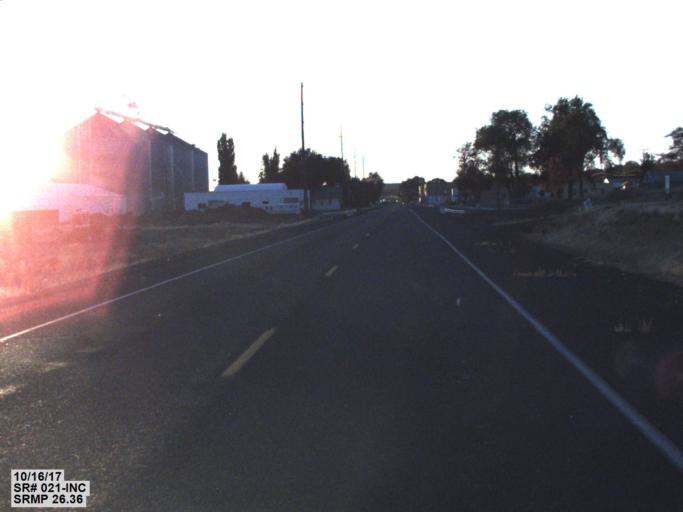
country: US
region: Washington
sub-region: Adams County
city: Ritzville
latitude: 46.9714
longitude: -118.6088
